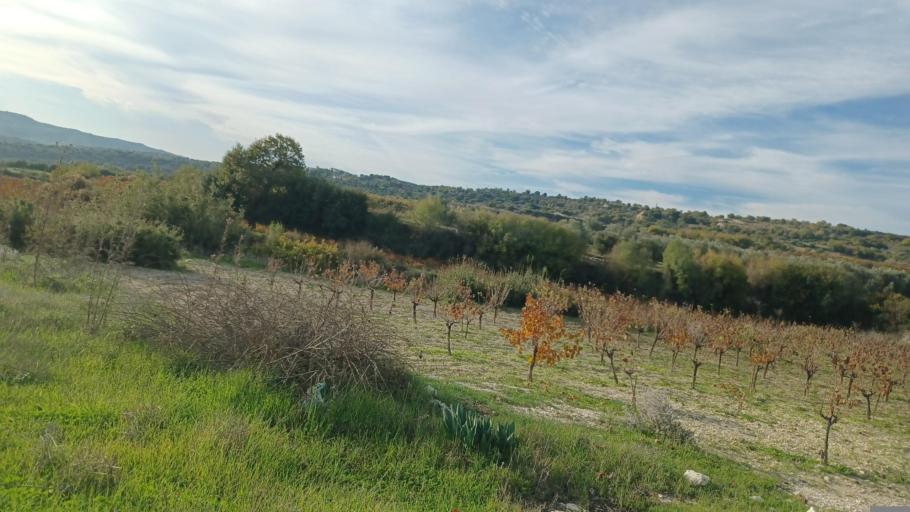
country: CY
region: Pafos
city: Mesogi
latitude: 34.8664
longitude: 32.5250
